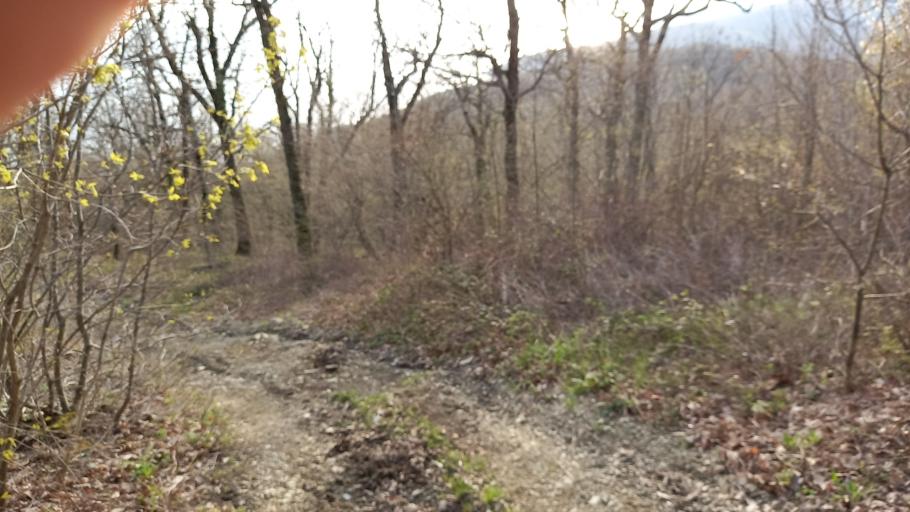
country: RU
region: Krasnodarskiy
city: Arkhipo-Osipovka
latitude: 44.3568
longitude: 38.5484
